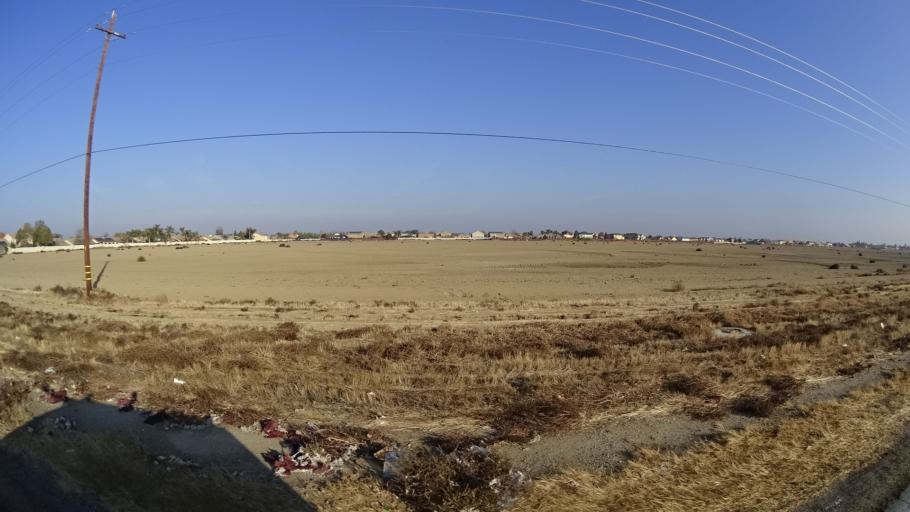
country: US
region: California
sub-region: Kern County
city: Greenacres
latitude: 35.2964
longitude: -119.1171
